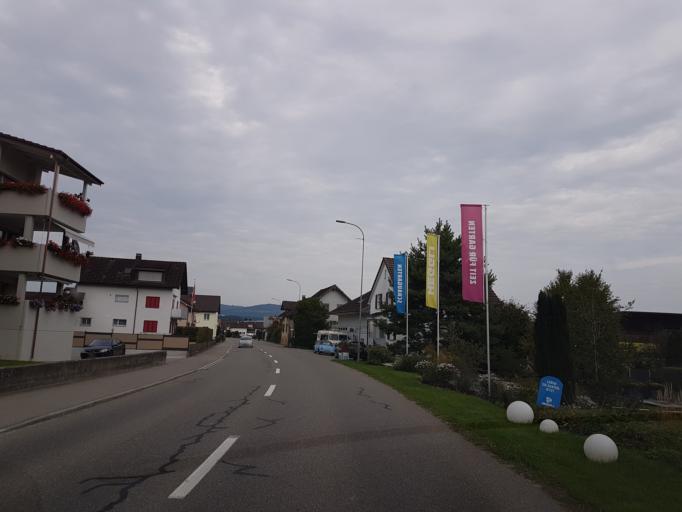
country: CH
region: Aargau
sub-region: Bezirk Muri
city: Merenschwand
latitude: 47.2592
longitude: 8.3802
